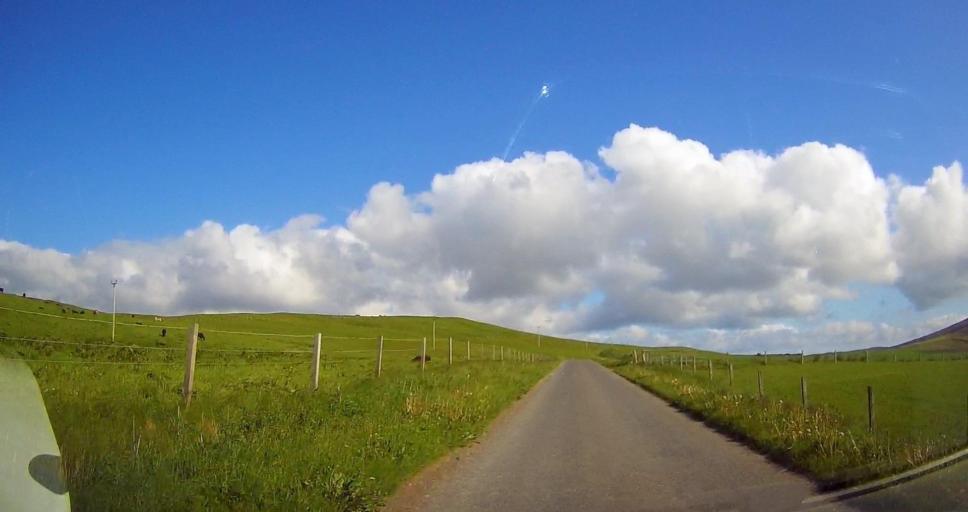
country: GB
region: Scotland
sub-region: Orkney Islands
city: Stromness
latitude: 58.9814
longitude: -3.1386
